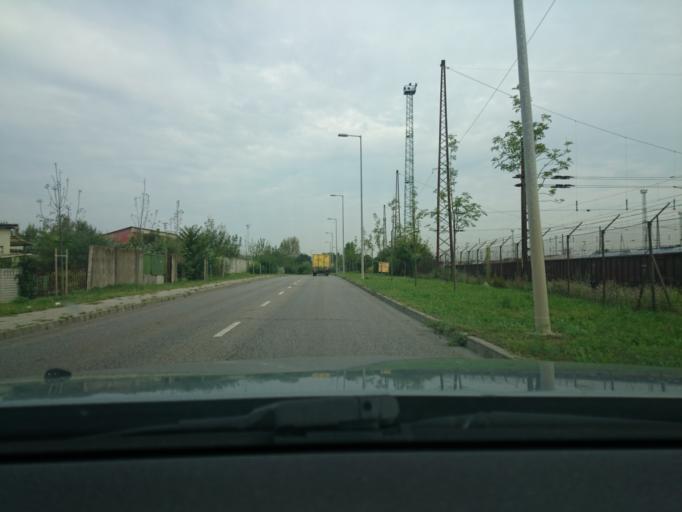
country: HU
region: Budapest
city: Budapest XX. keruelet
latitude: 47.4565
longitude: 19.0964
